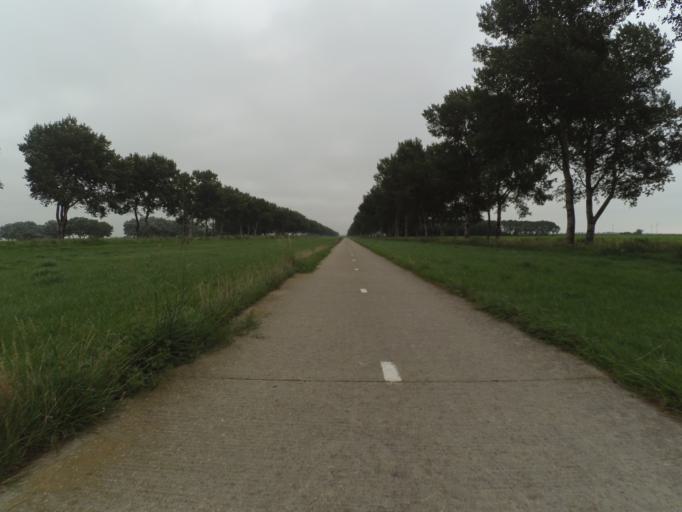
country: NL
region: Flevoland
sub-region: Gemeente Zeewolde
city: Zeewolde
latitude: 52.3936
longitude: 5.4522
